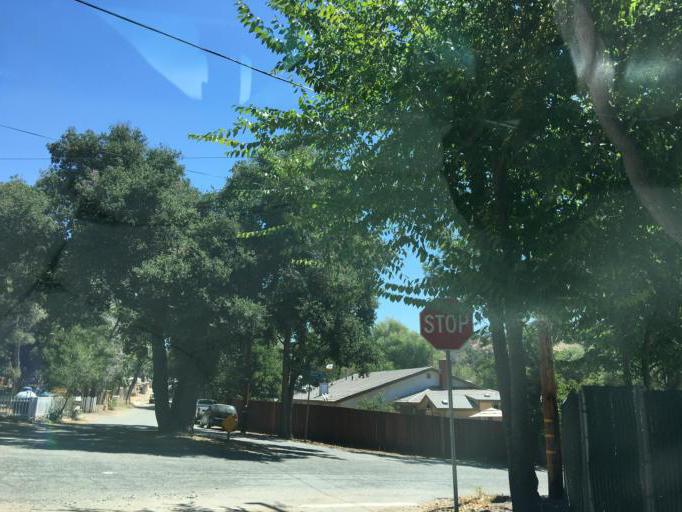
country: US
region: California
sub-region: Los Angeles County
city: Agua Dulce
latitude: 34.5091
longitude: -118.3659
